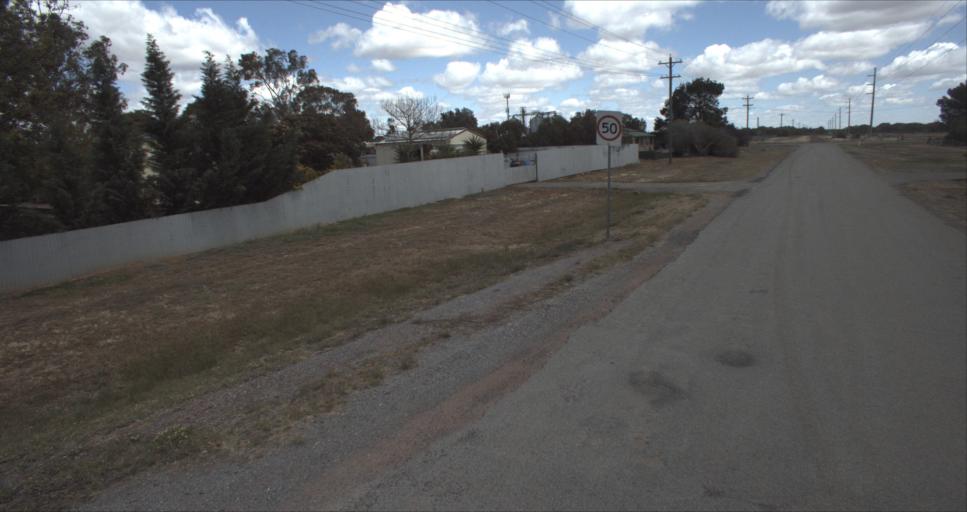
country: AU
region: New South Wales
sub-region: Murrumbidgee Shire
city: Darlington Point
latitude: -34.5123
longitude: 146.1859
